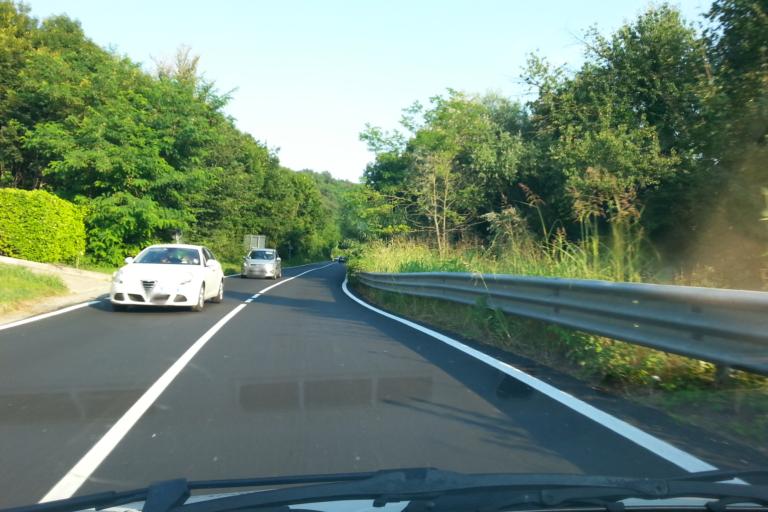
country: IT
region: Piedmont
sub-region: Provincia di Torino
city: Avigliana
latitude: 45.0593
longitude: 7.3931
